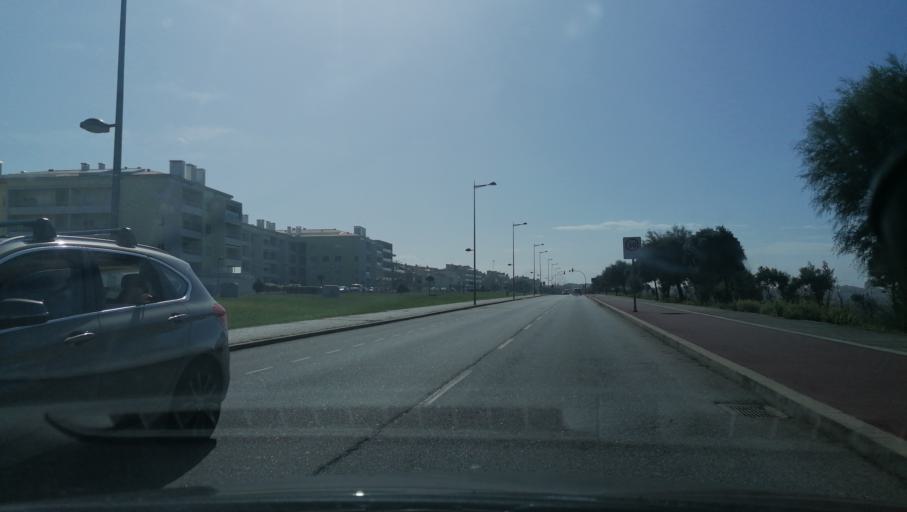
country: PT
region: Aveiro
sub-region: Espinho
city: Espinho
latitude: 41.0236
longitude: -8.6425
